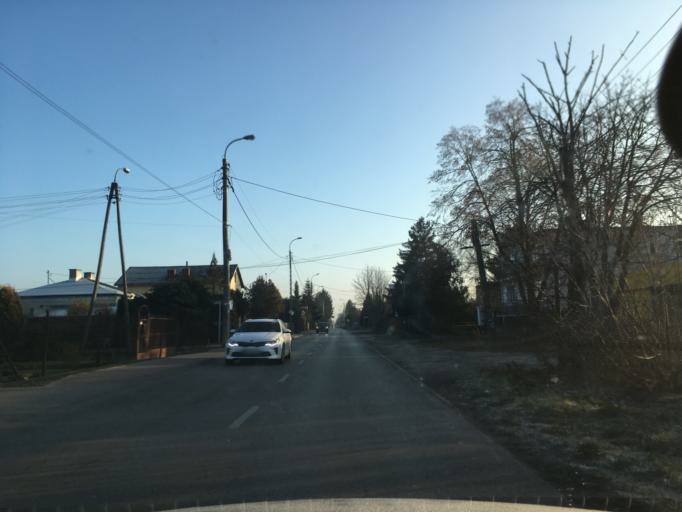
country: PL
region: Masovian Voivodeship
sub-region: Powiat piaseczynski
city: Piaseczno
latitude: 52.0698
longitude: 20.9941
